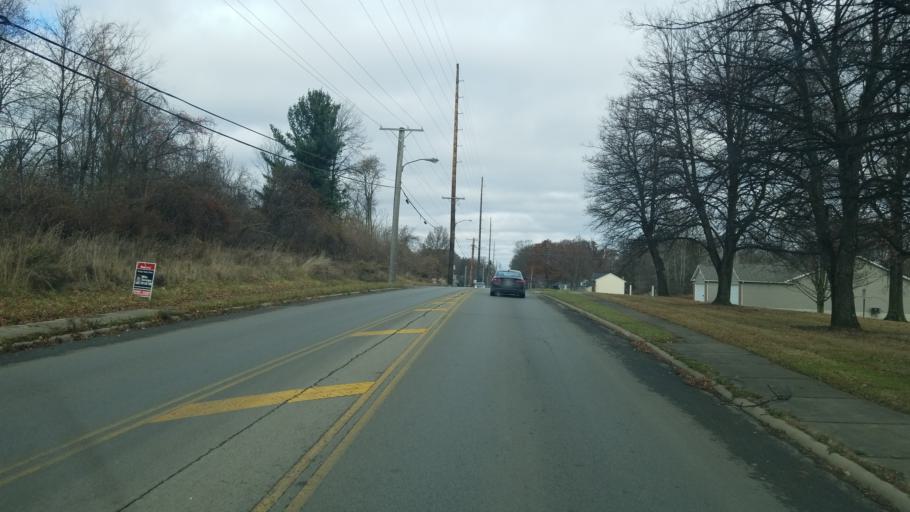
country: US
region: Ohio
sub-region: Richland County
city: Mansfield
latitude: 40.7484
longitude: -82.5517
